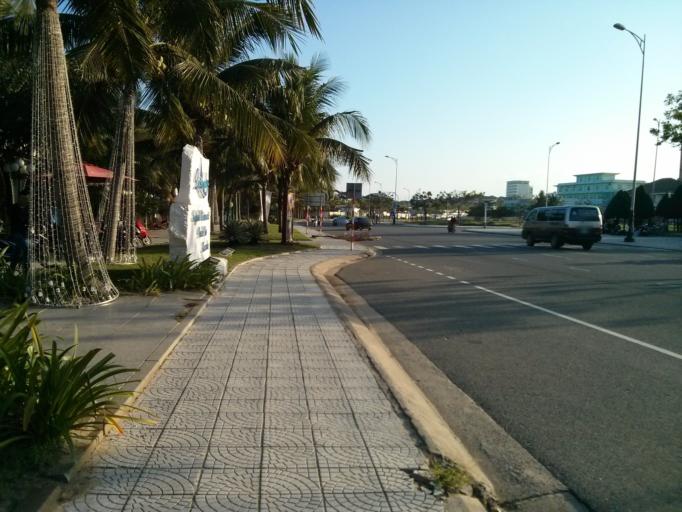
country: VN
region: Da Nang
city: Son Tra
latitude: 16.0482
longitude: 108.2493
